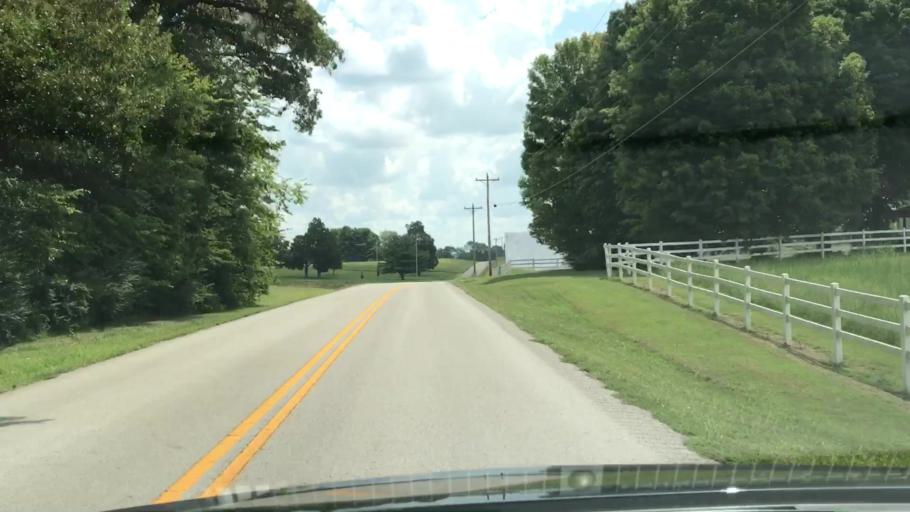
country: US
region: Kentucky
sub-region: Todd County
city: Elkton
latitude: 36.7871
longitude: -87.1319
